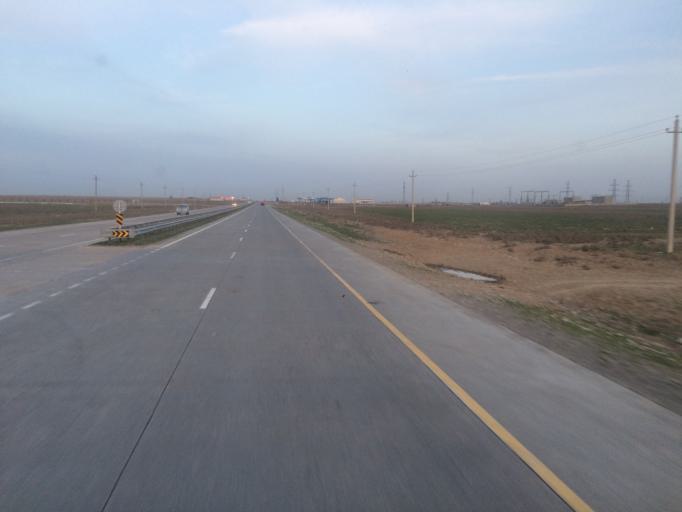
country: KZ
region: Ongtustik Qazaqstan
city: Shymkent
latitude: 42.4569
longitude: 69.6016
